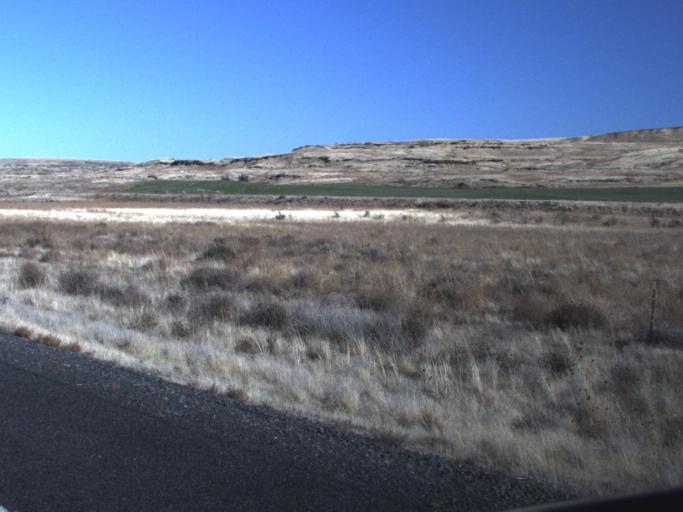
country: US
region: Washington
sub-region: Franklin County
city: Connell
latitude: 46.6910
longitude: -118.4318
